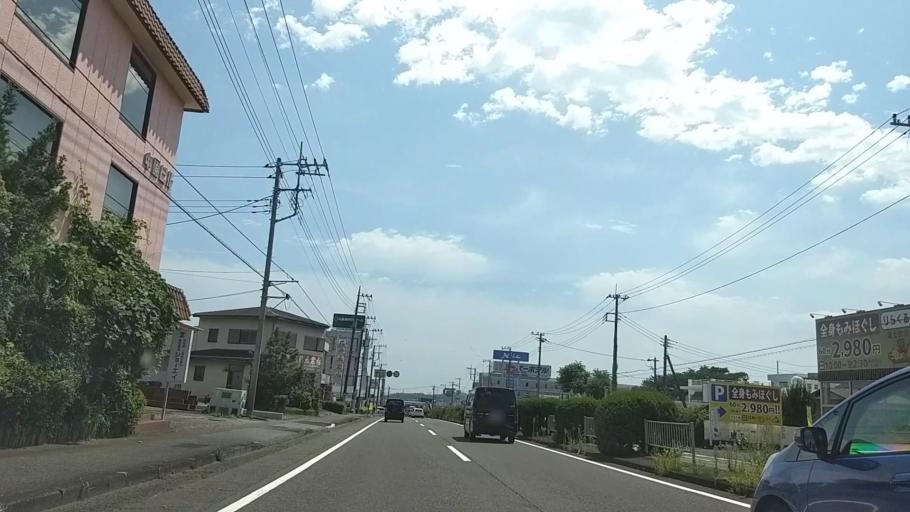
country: JP
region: Shizuoka
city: Fujinomiya
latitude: 35.2357
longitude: 138.6205
